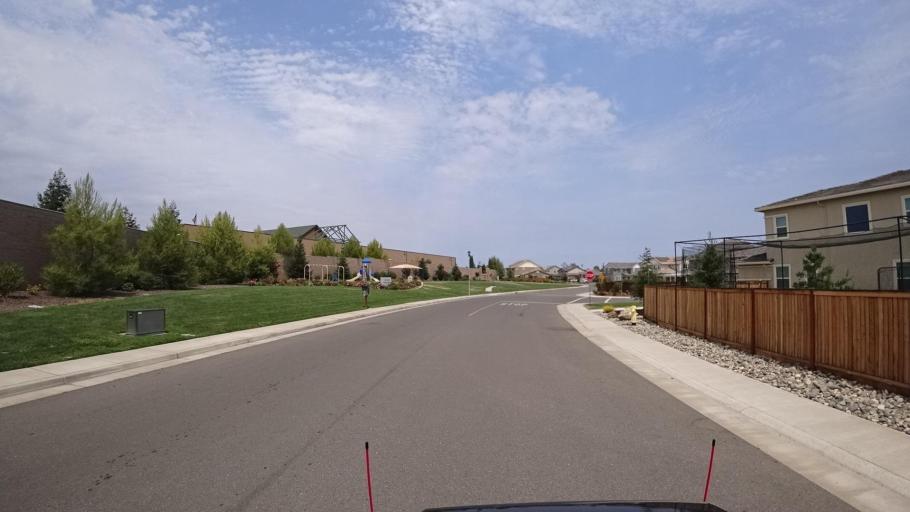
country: US
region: California
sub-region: Placer County
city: Loomis
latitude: 38.8034
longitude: -121.2007
